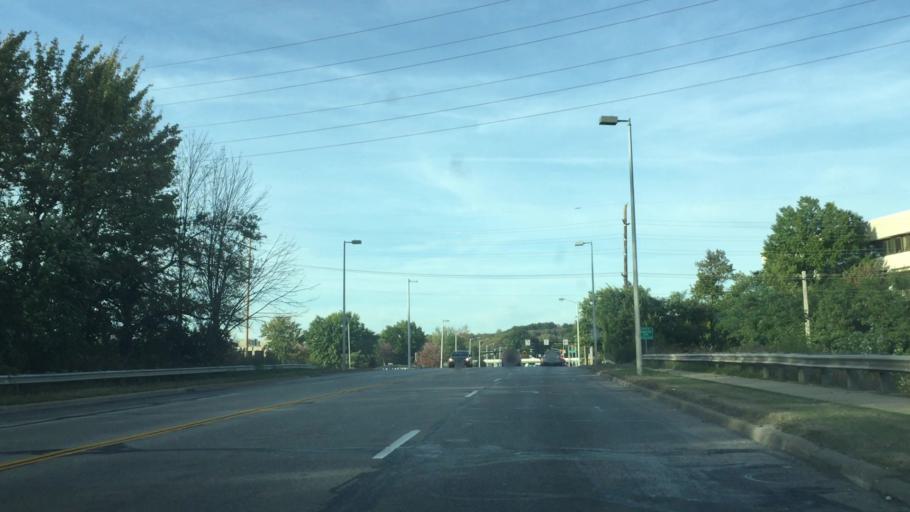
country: US
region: Ohio
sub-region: Cuyahoga County
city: Solon
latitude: 41.4016
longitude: -81.4684
